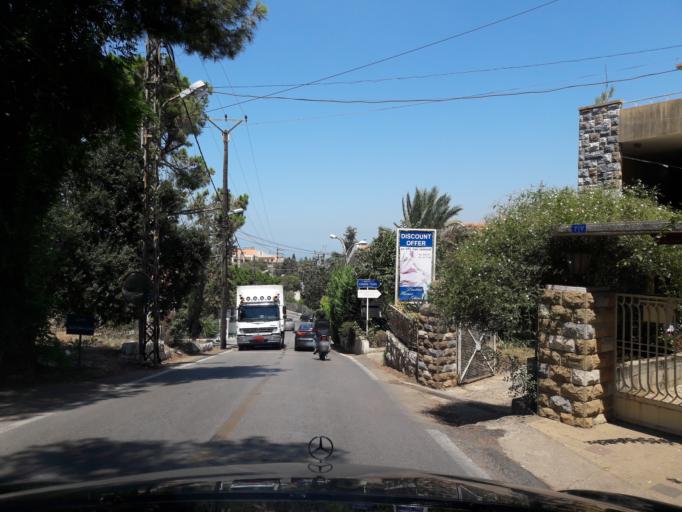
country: LB
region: Mont-Liban
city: Djounie
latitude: 33.9296
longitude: 35.6255
